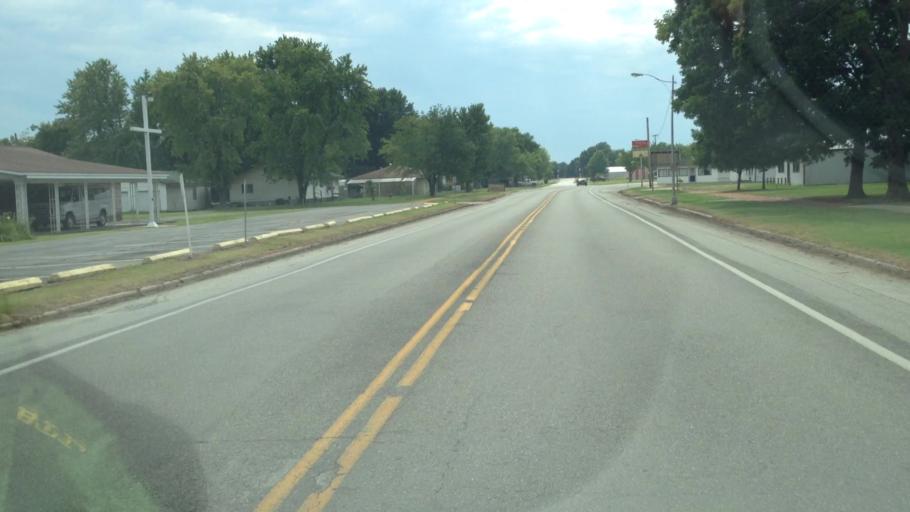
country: US
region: Kansas
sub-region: Labette County
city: Chetopa
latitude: 37.0369
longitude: -95.0961
